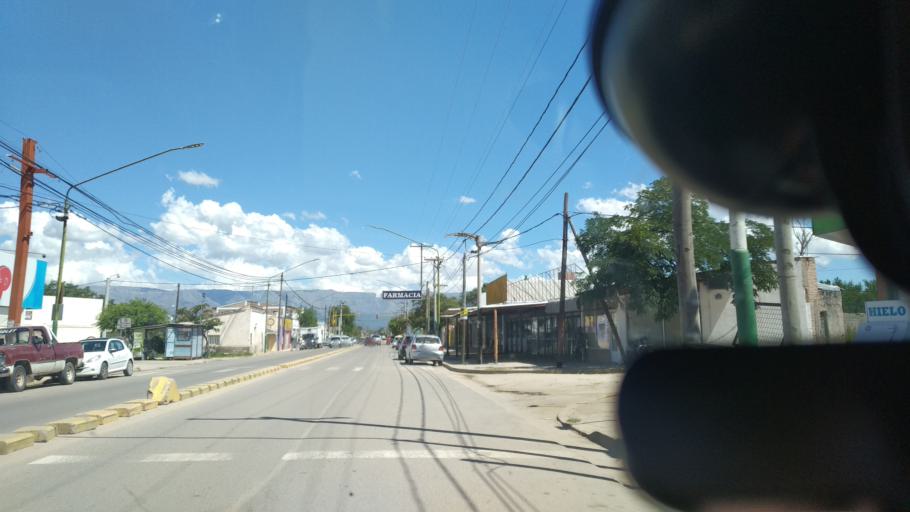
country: AR
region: Cordoba
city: Villa Cura Brochero
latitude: -31.7097
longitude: -65.0162
